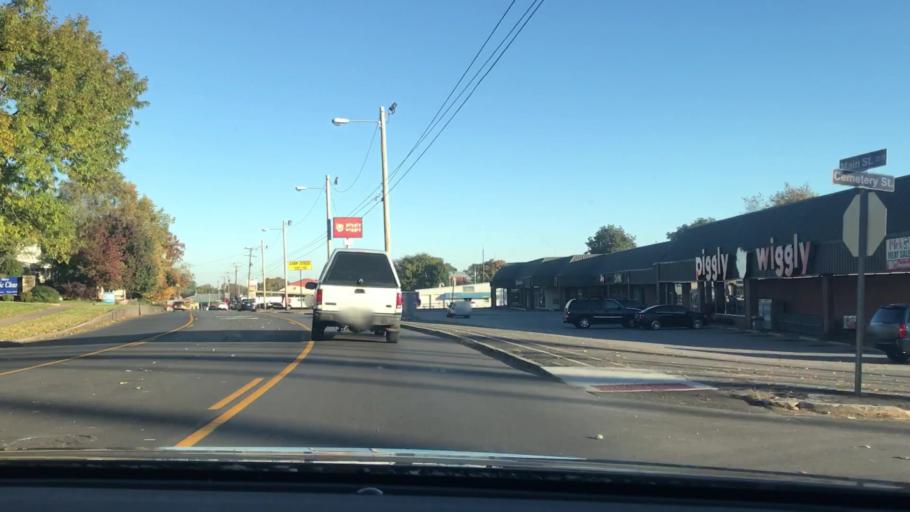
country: US
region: Kentucky
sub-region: Simpson County
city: Franklin
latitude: 36.7256
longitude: -86.5773
